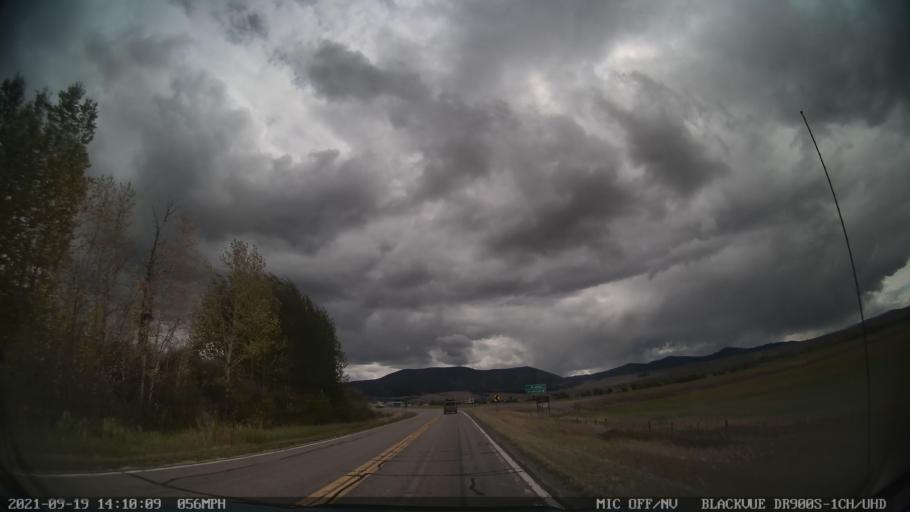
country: US
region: Montana
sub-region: Lewis and Clark County
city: Lincoln
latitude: 46.8767
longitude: -112.9316
